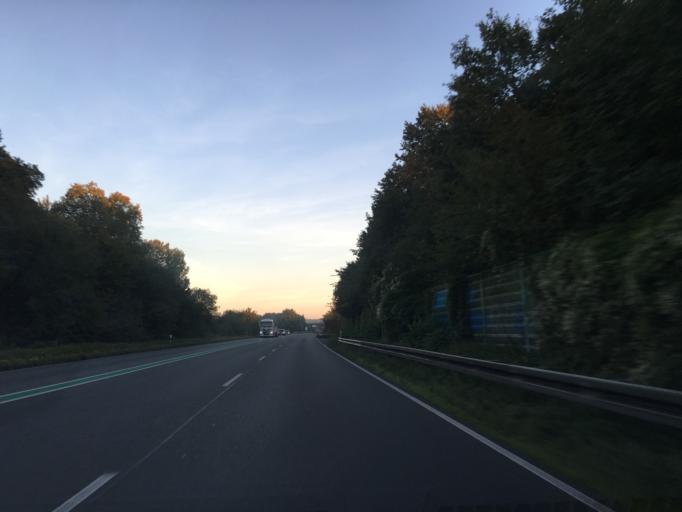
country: DE
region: North Rhine-Westphalia
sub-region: Regierungsbezirk Munster
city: Steinfurt
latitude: 52.1174
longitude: 7.3705
